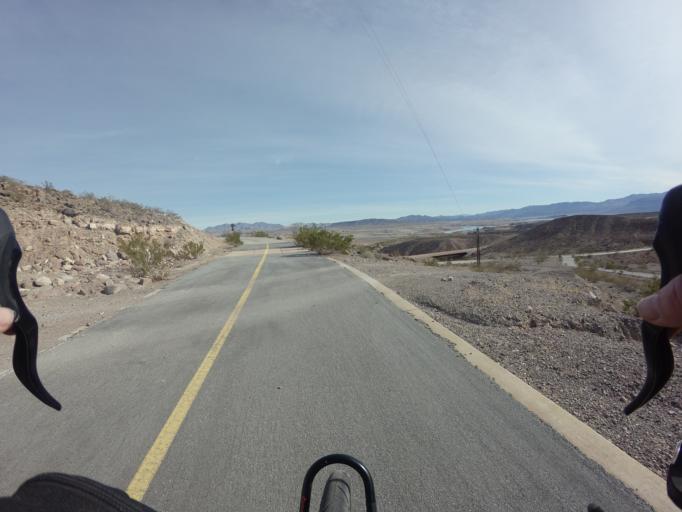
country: US
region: Nevada
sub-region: Clark County
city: Henderson
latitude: 36.1140
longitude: -114.8676
